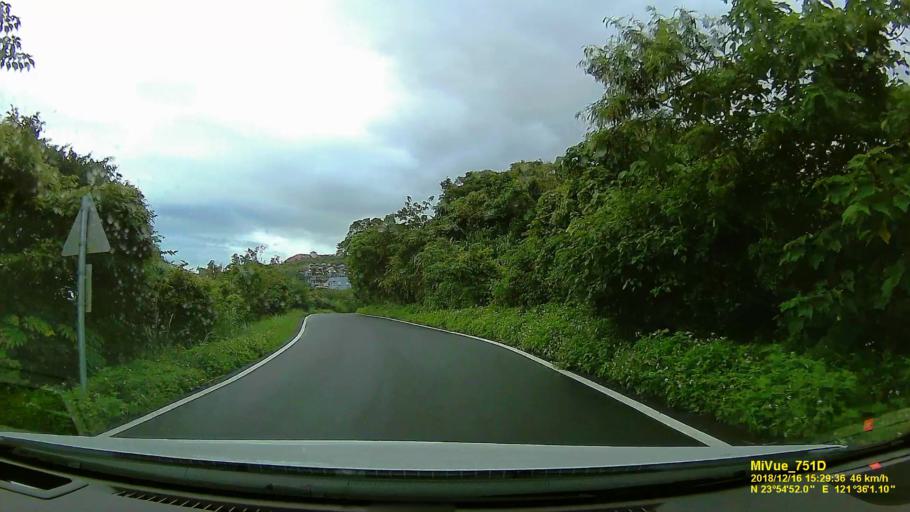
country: TW
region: Taiwan
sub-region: Hualien
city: Hualian
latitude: 23.9143
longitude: 121.6001
